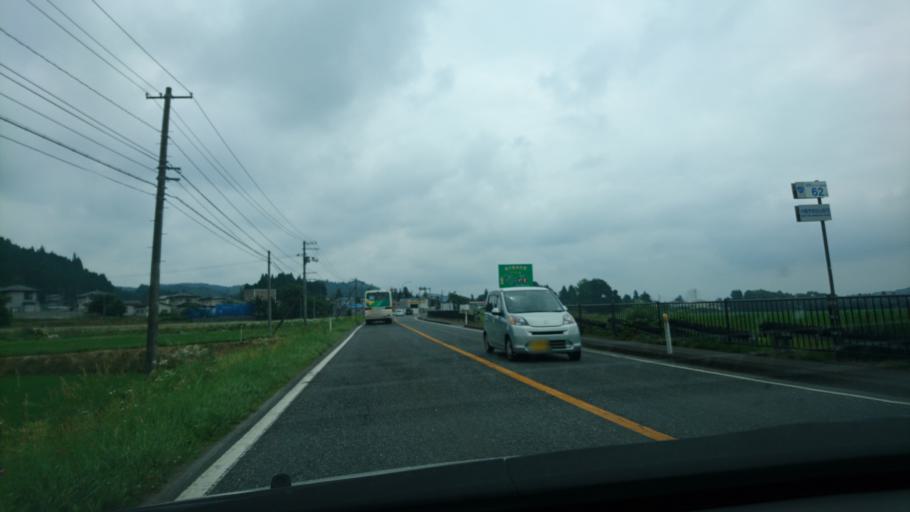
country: JP
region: Miyagi
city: Furukawa
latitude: 38.7140
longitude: 140.8276
